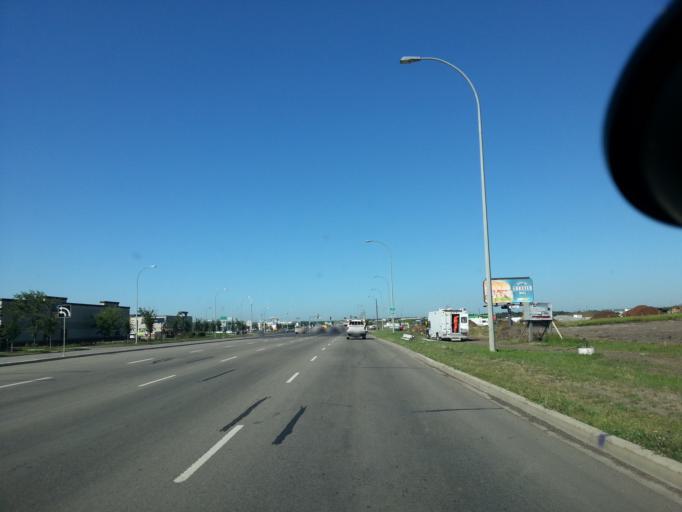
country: CA
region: Alberta
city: St. Albert
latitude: 53.5995
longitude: -113.5707
